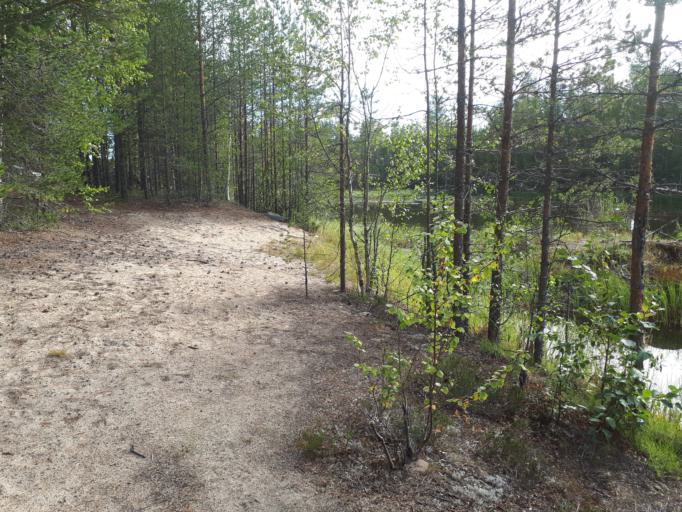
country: FI
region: Northern Ostrobothnia
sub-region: Oulunkaari
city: Ii
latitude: 65.2896
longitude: 25.3819
